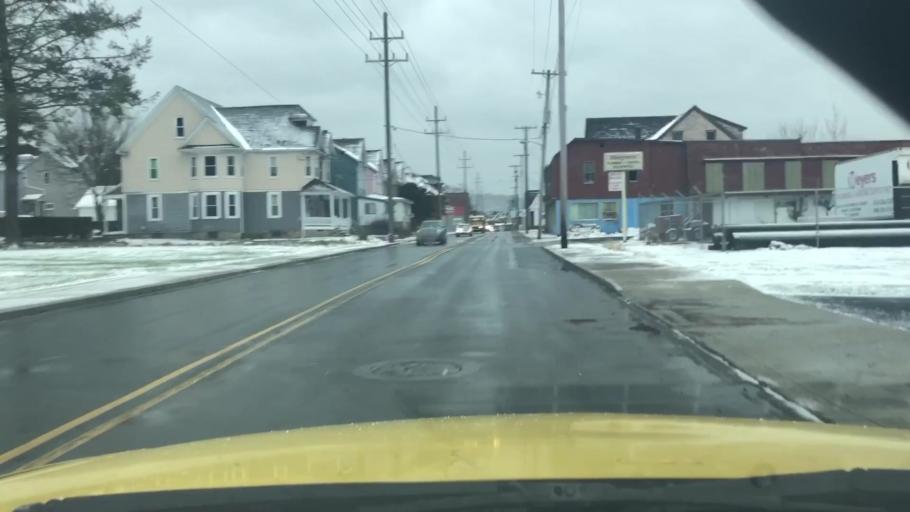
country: US
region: Pennsylvania
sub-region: Cambria County
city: Dale
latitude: 40.3123
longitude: -78.9123
